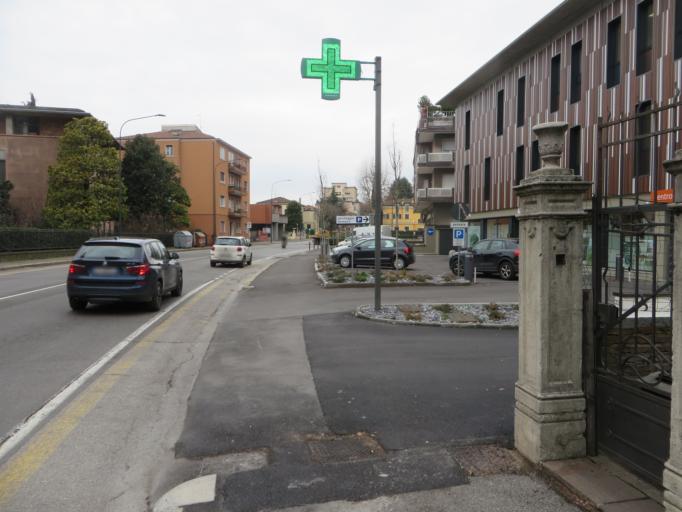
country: IT
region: Lombardy
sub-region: Provincia di Brescia
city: Brescia
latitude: 45.5315
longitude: 10.2463
